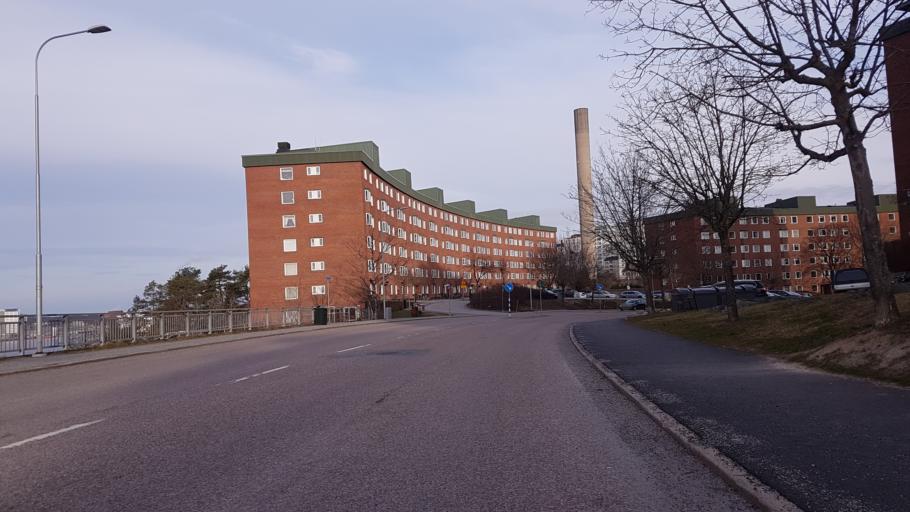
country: SE
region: Stockholm
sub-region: Lidingo
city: Lidingoe
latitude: 59.3473
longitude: 18.1423
